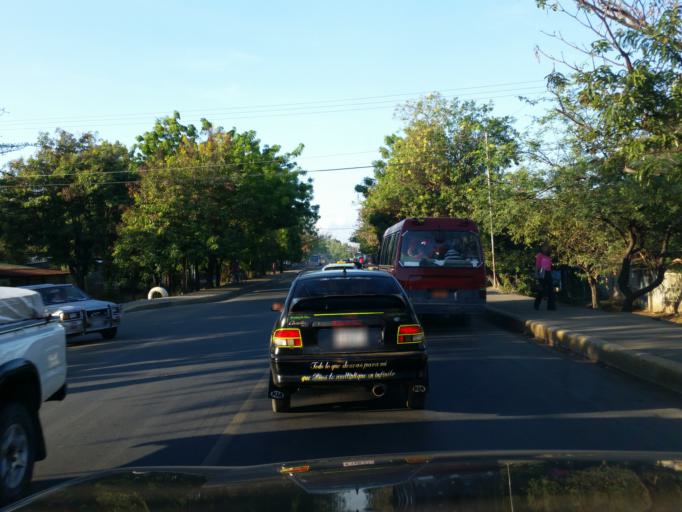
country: NI
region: Managua
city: Tipitapa
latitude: 12.1798
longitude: -86.0960
